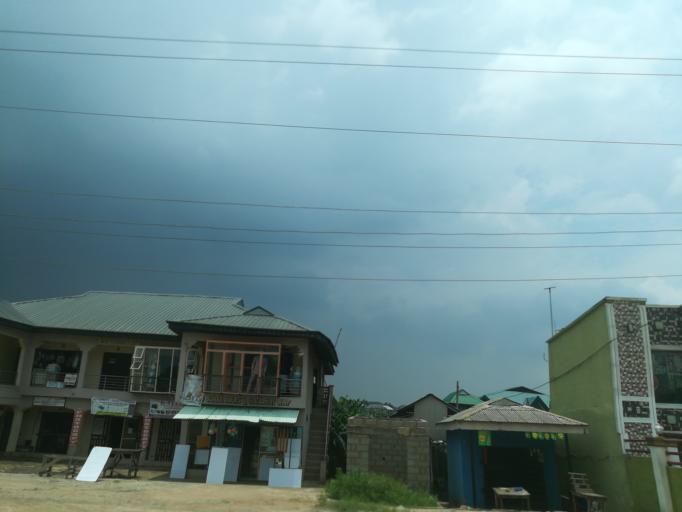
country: NG
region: Lagos
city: Ikorodu
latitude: 6.6100
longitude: 3.5819
